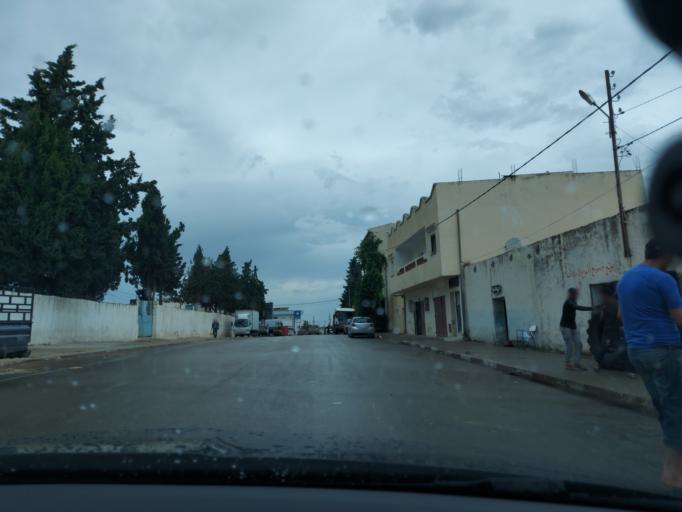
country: TN
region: Silyanah
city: Maktar
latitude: 35.8557
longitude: 9.2033
